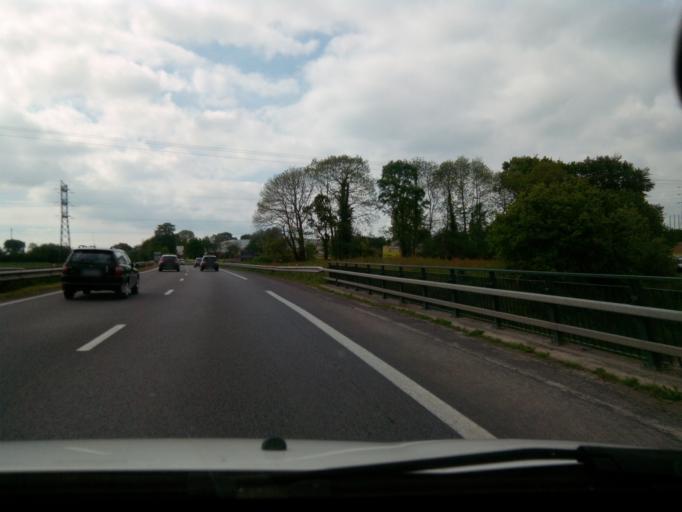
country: FR
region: Brittany
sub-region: Departement des Cotes-d'Armor
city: Graces
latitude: 48.5623
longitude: -3.1878
